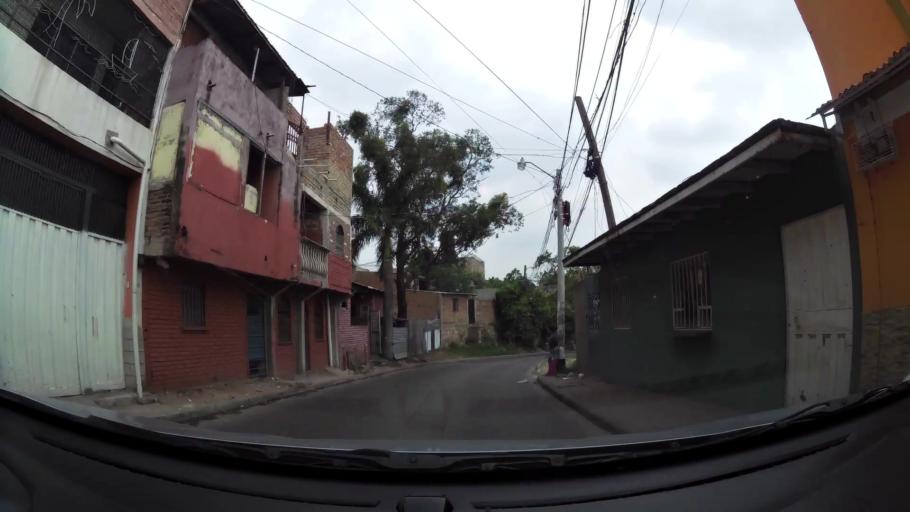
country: HN
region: Francisco Morazan
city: Tegucigalpa
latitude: 14.0986
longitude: -87.1707
